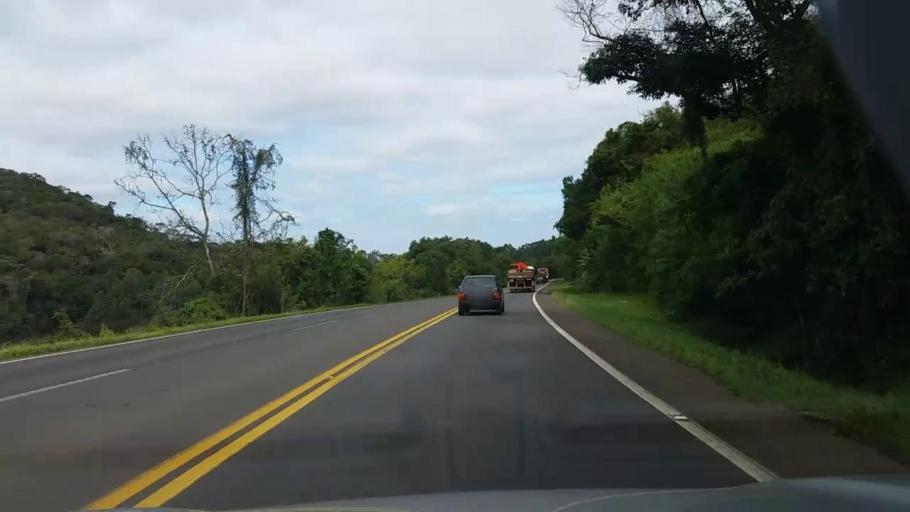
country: BR
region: Rio Grande do Sul
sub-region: Arroio Do Meio
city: Arroio do Meio
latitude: -29.3905
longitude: -52.0419
